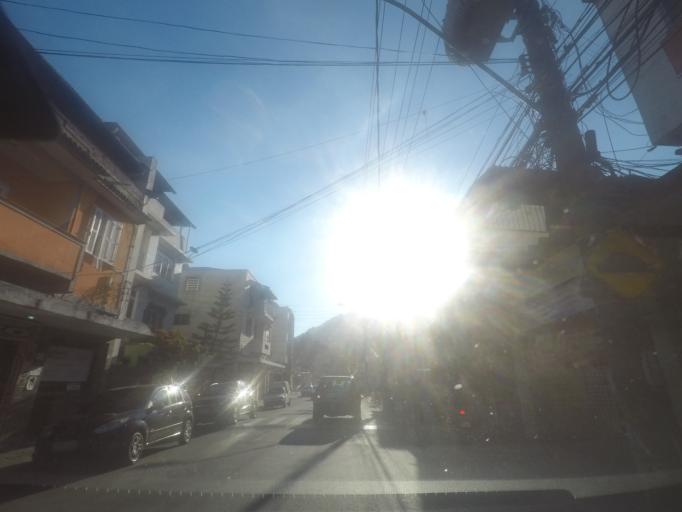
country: BR
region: Rio de Janeiro
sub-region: Petropolis
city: Petropolis
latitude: -22.4891
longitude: -43.1531
